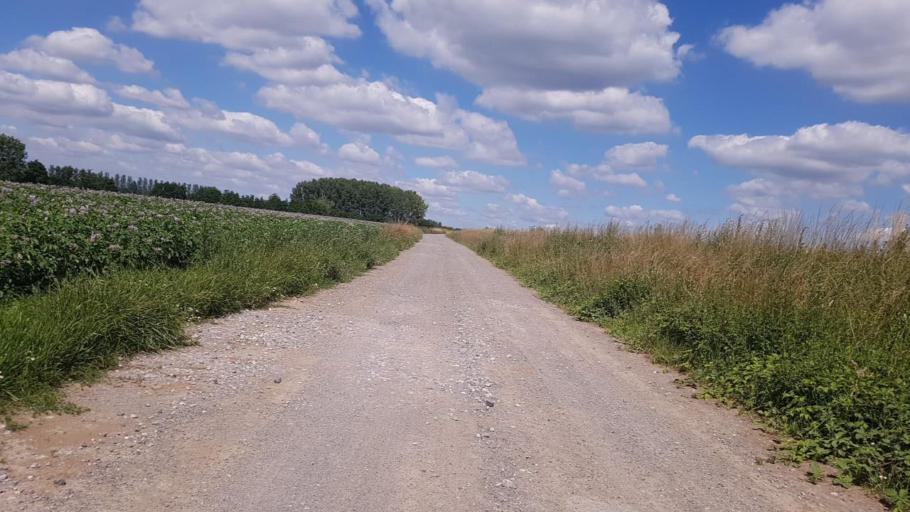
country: BE
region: Wallonia
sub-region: Province du Hainaut
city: Thuin
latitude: 50.3181
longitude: 4.3563
